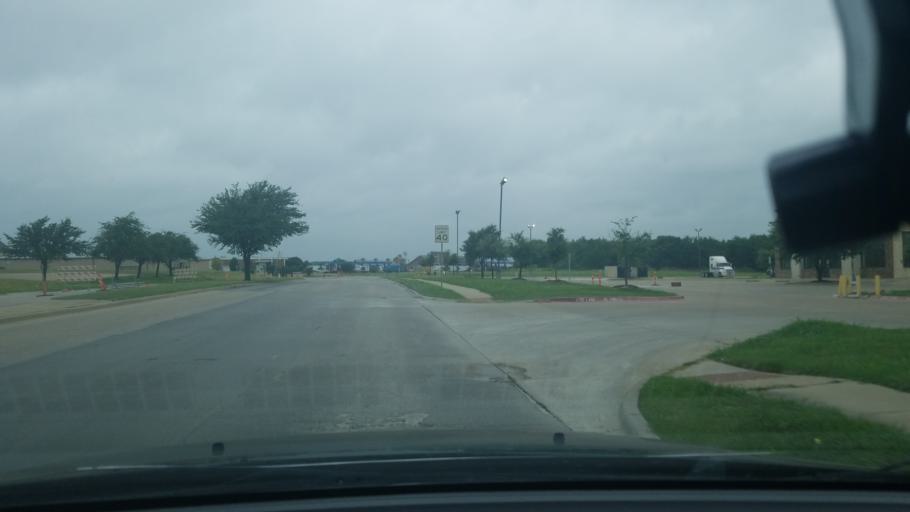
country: US
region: Texas
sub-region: Dallas County
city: Mesquite
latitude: 32.7883
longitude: -96.6536
